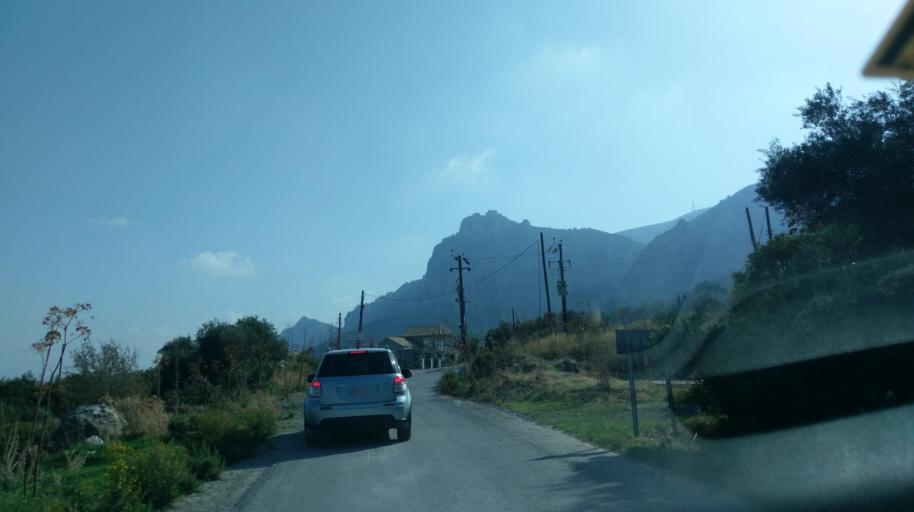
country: CY
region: Keryneia
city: Kyrenia
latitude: 35.3218
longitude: 33.2601
